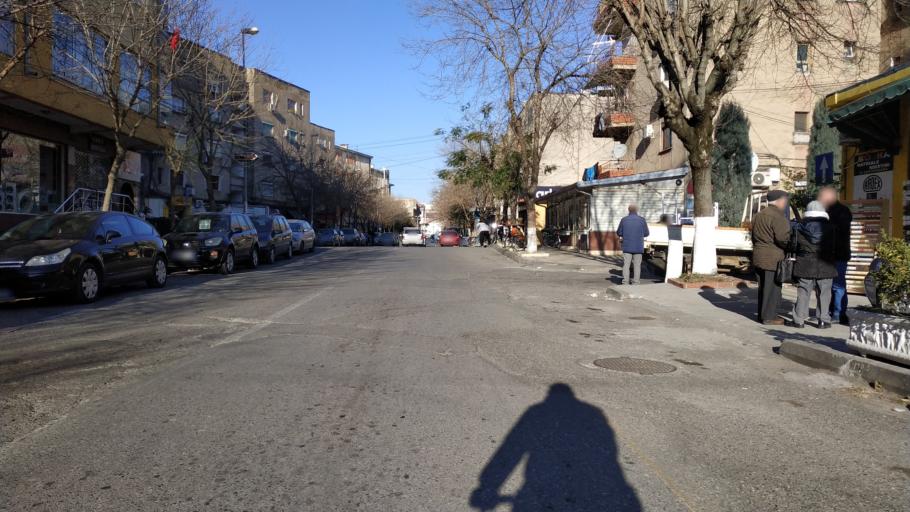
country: AL
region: Shkoder
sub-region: Rrethi i Shkodres
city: Shkoder
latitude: 42.0633
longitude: 19.5104
